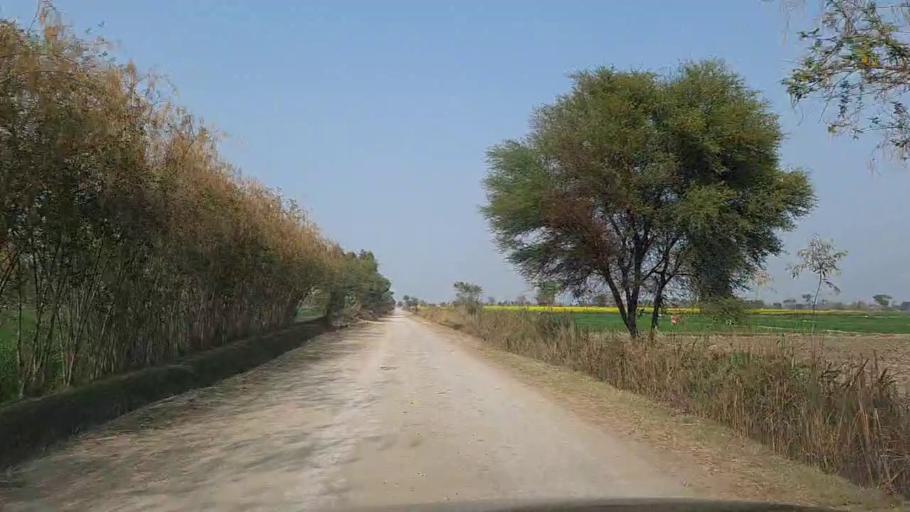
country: PK
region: Sindh
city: Daur
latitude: 26.3989
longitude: 68.4239
